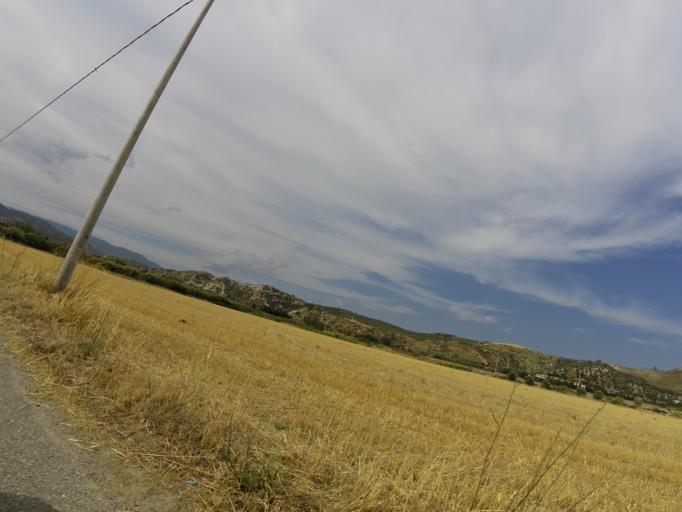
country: IT
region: Calabria
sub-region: Provincia di Reggio Calabria
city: Monasterace
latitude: 38.4523
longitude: 16.5189
